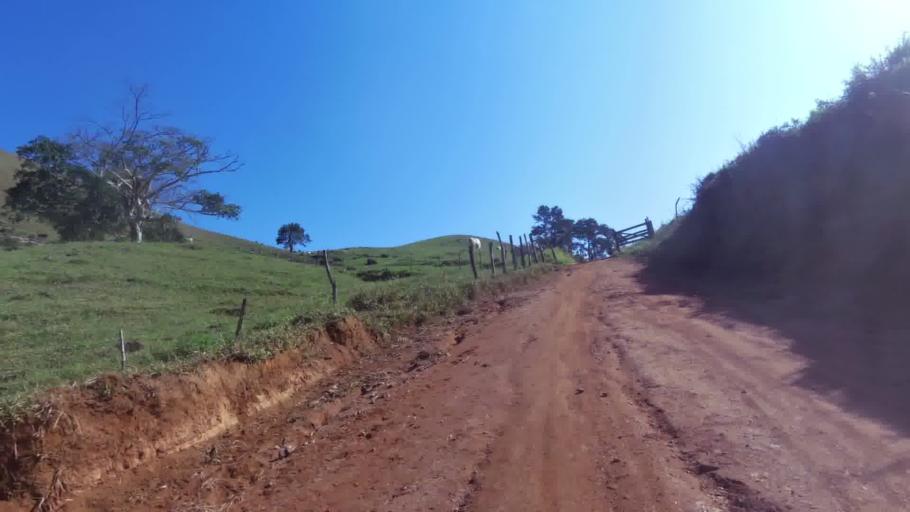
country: BR
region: Espirito Santo
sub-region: Alfredo Chaves
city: Alfredo Chaves
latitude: -20.6817
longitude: -40.7816
